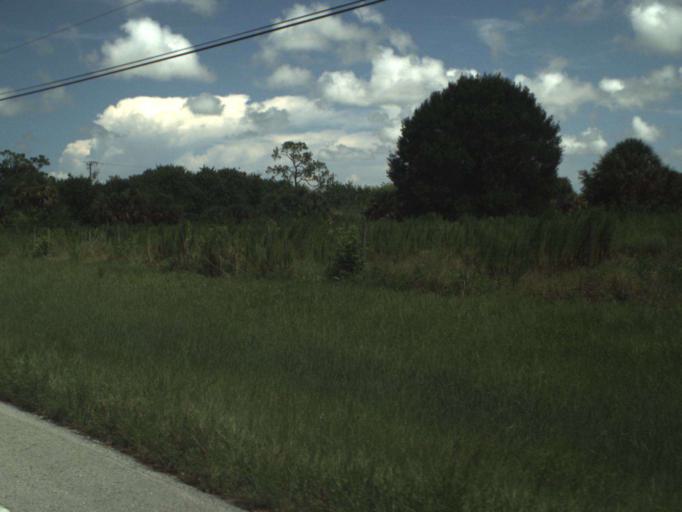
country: US
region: Florida
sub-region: Indian River County
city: Sebastian
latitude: 27.7488
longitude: -80.5004
